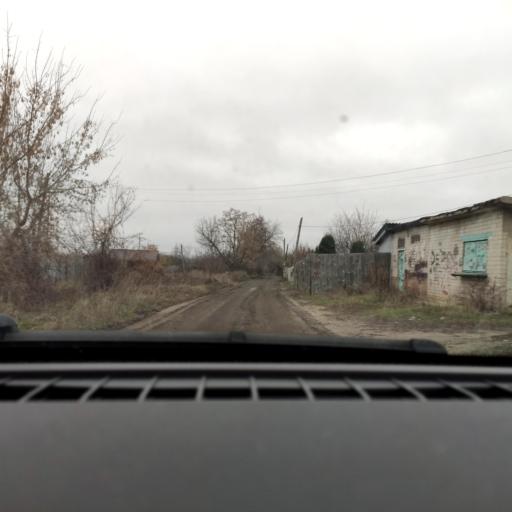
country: RU
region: Voronezj
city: Maslovka
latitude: 51.6100
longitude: 39.2726
